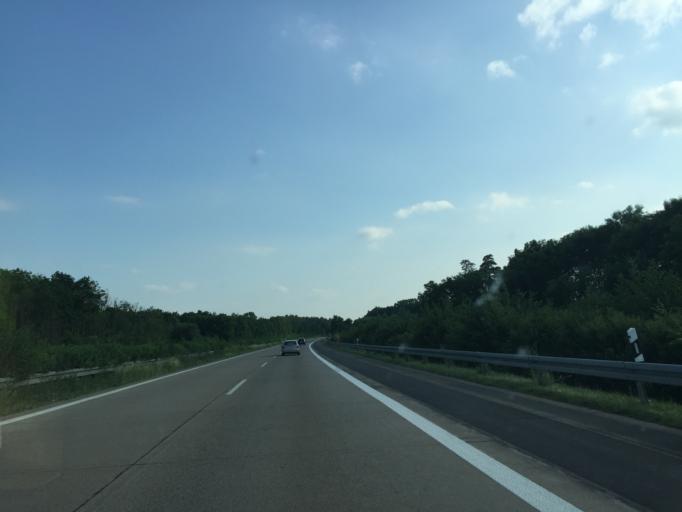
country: DE
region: Baden-Wuerttemberg
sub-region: Karlsruhe Region
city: Osterburken
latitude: 49.3937
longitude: 9.4696
